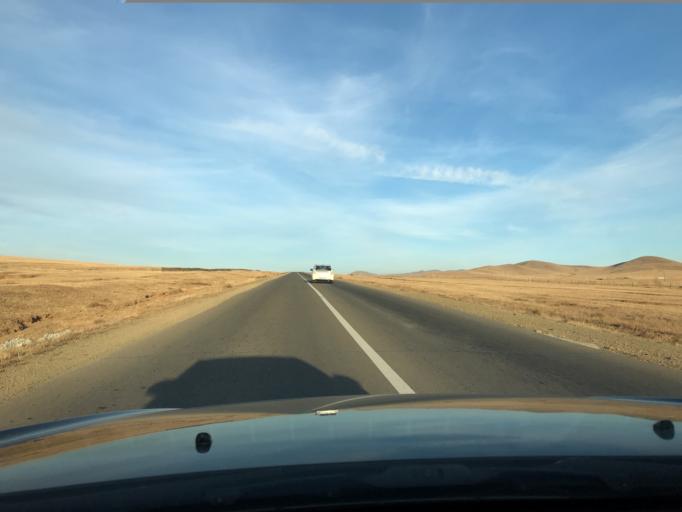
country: MN
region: Central Aimak
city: Arhust
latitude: 47.7953
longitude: 107.4975
